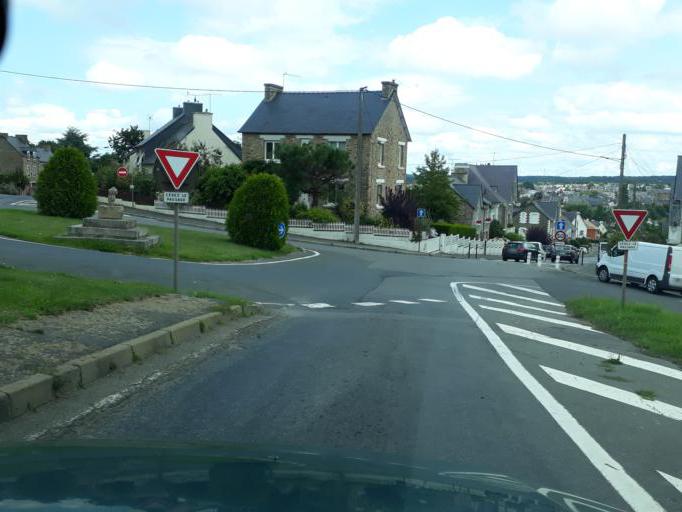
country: FR
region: Brittany
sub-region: Departement des Cotes-d'Armor
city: Lamballe
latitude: 48.4623
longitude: -2.5238
